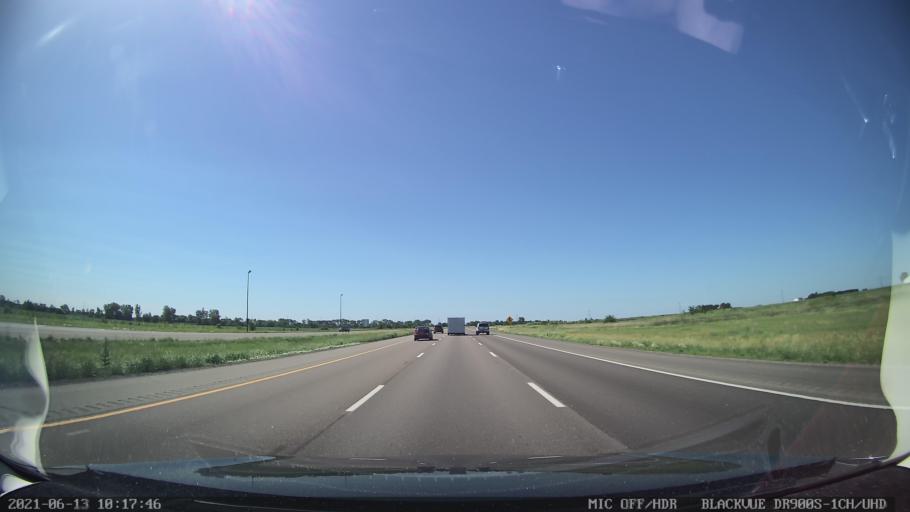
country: US
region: Illinois
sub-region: Logan County
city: Lincoln
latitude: 40.1092
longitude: -89.4174
